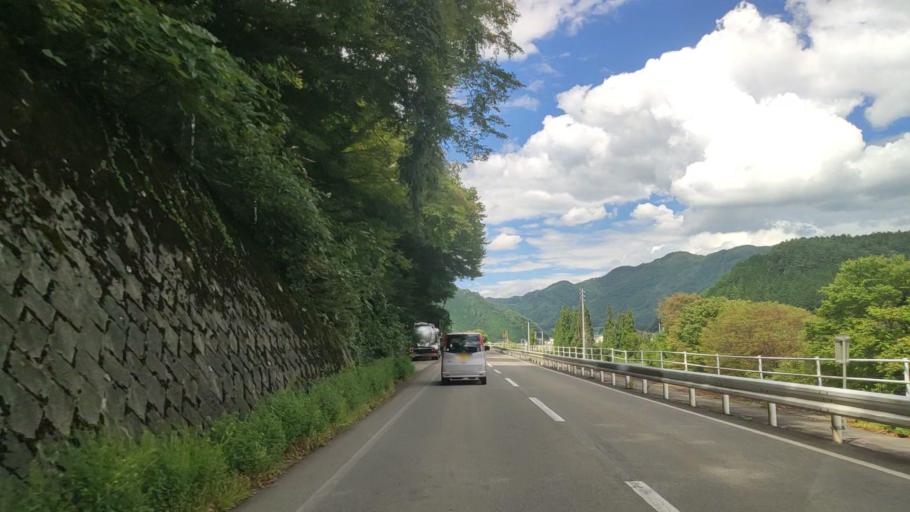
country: JP
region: Gifu
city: Takayama
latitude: 36.1794
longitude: 137.2614
